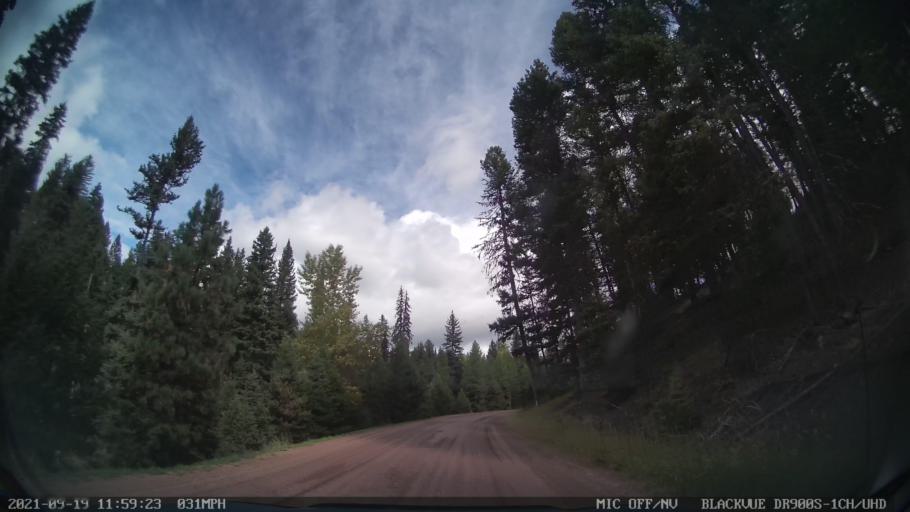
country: US
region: Montana
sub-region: Missoula County
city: Seeley Lake
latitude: 47.1851
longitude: -113.4775
